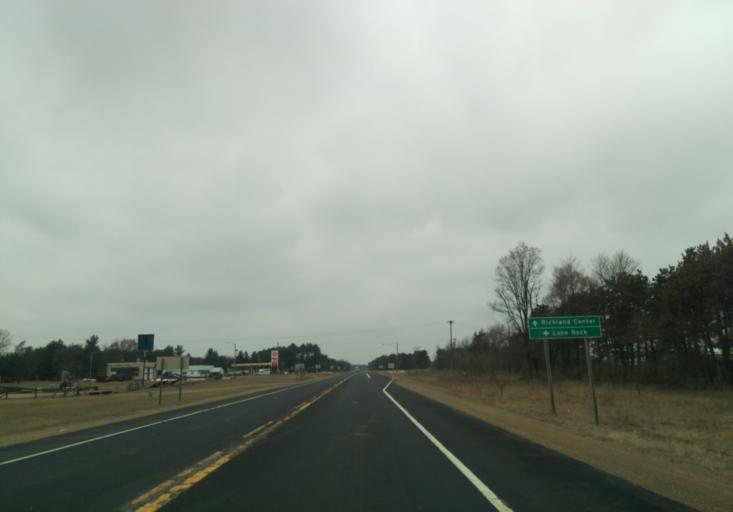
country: US
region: Wisconsin
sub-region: Sauk County
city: Spring Green
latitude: 43.1913
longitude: -90.1962
